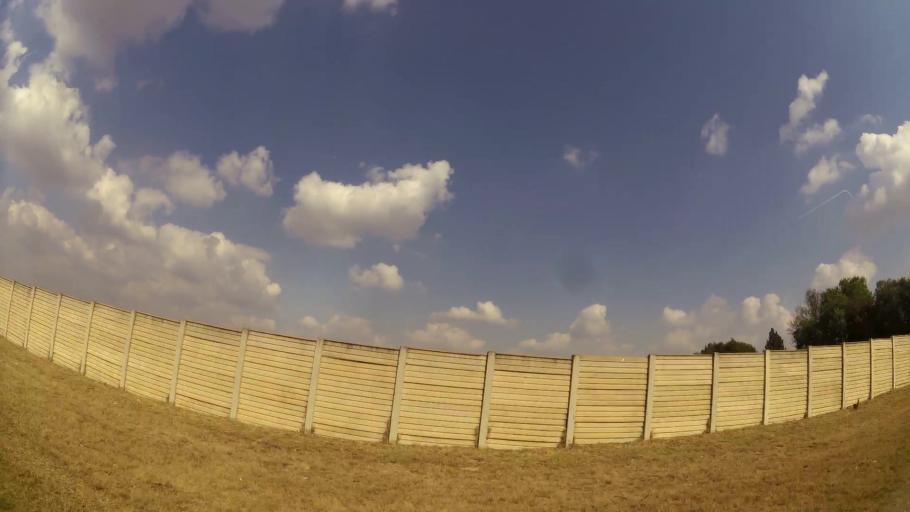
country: ZA
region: Mpumalanga
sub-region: Nkangala District Municipality
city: Delmas
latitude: -26.1502
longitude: 28.5593
